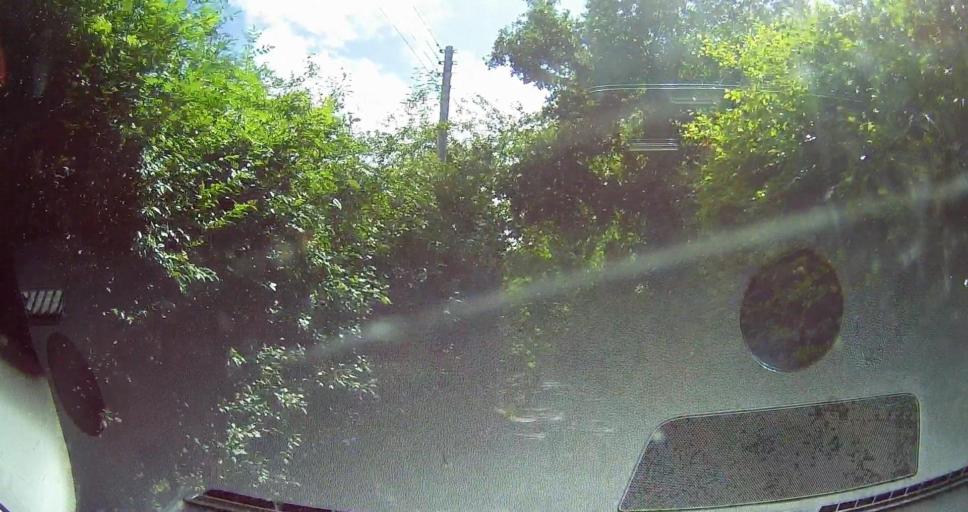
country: GB
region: England
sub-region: Kent
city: Borough Green
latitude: 51.2891
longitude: 0.3108
